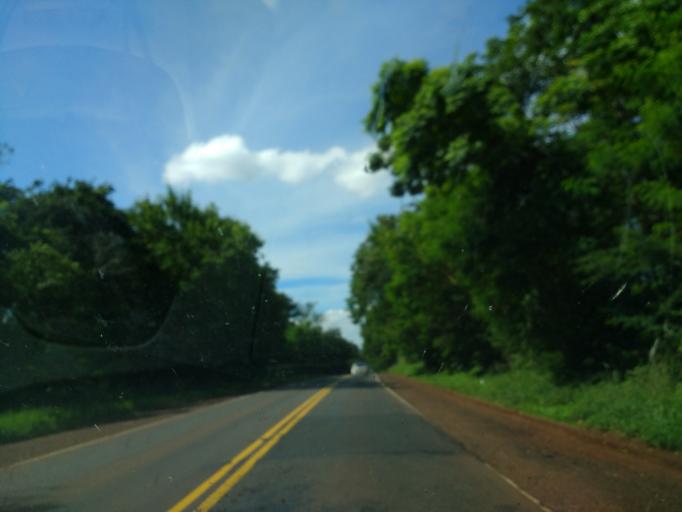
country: BR
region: Parana
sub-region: Engenheiro Beltrao
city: Engenheiro Beltrao
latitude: -23.5684
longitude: -52.2626
